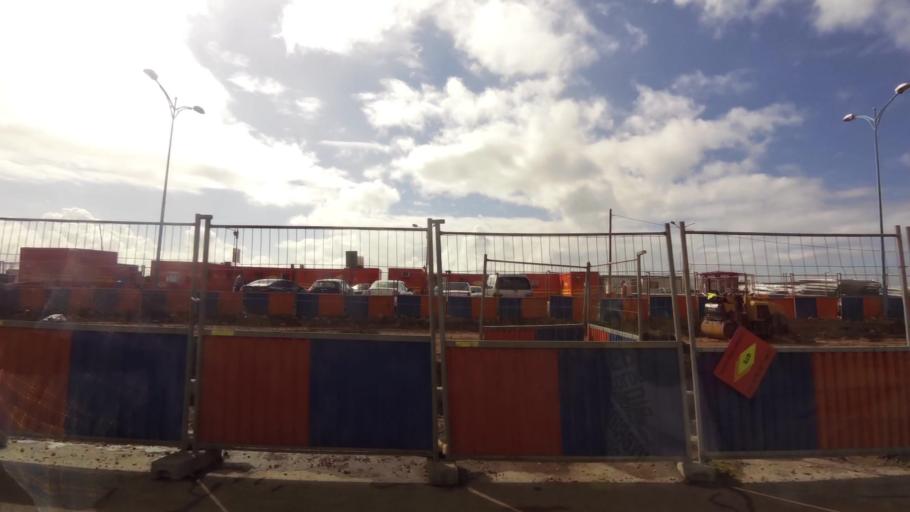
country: MA
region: Grand Casablanca
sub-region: Casablanca
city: Casablanca
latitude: 33.5796
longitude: -7.7036
